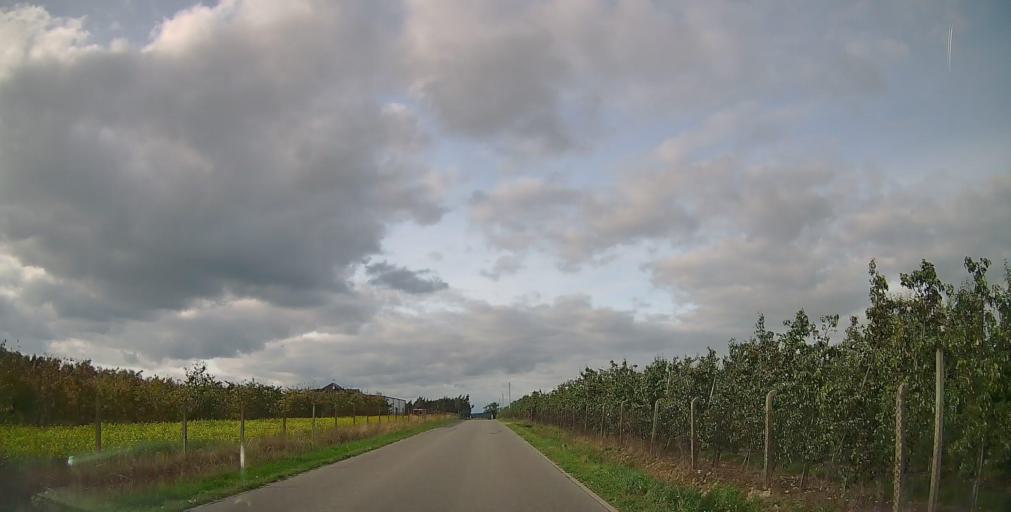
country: PL
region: Masovian Voivodeship
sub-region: Powiat bialobrzeski
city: Promna
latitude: 51.7498
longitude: 20.9626
